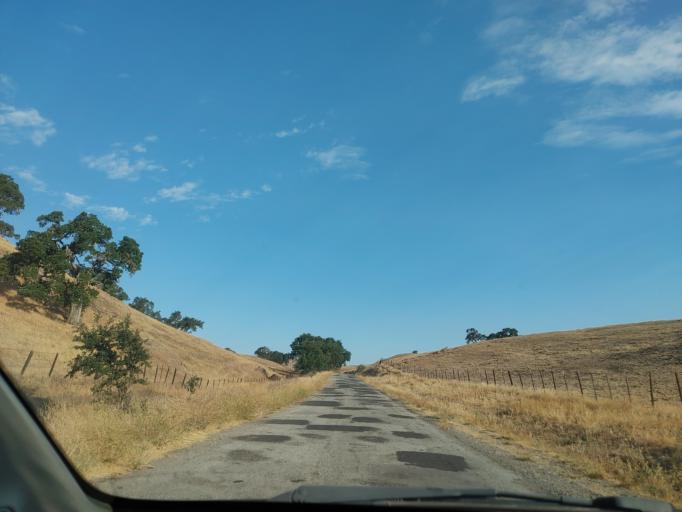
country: US
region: California
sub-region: San Benito County
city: Ridgemark
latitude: 36.7555
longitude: -121.1663
